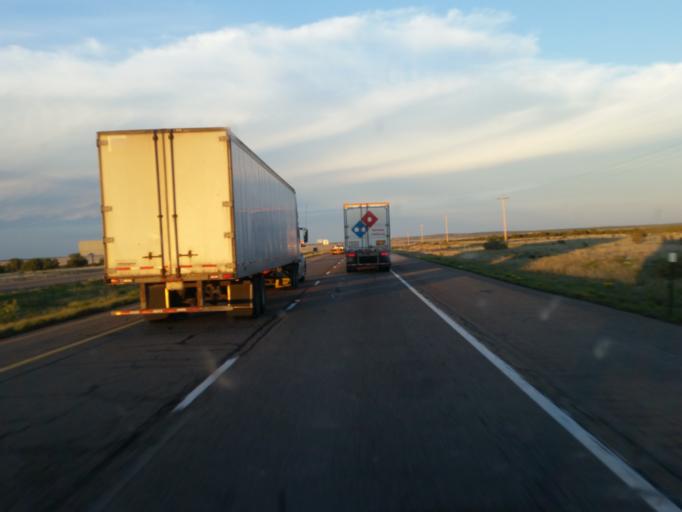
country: US
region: New Mexico
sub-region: San Miguel County
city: Las Vegas
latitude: 34.9930
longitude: -105.3286
